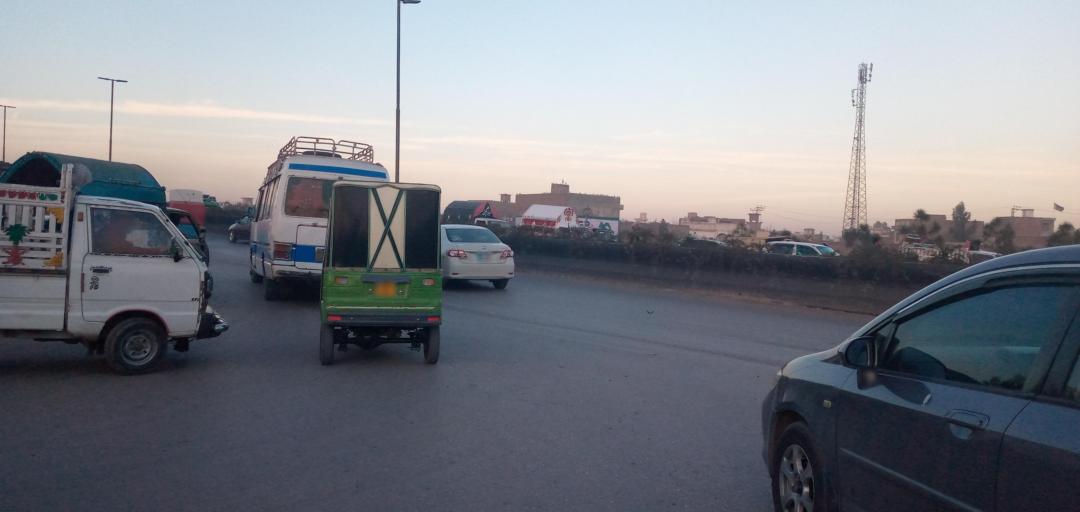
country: PK
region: Khyber Pakhtunkhwa
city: Peshawar
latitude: 34.0176
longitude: 71.6218
